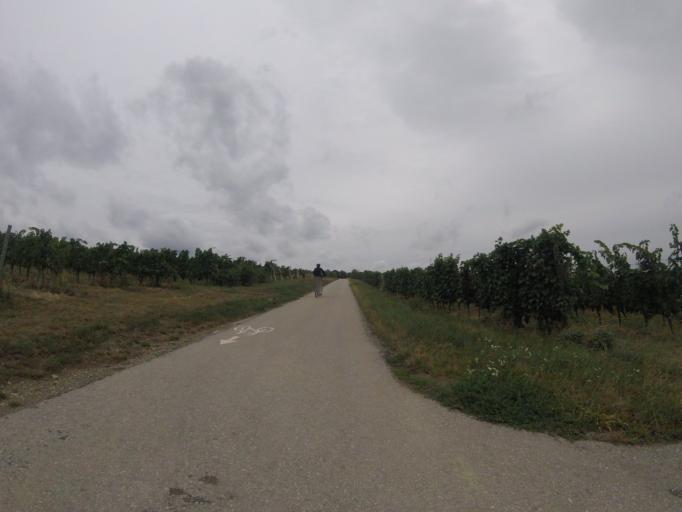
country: AT
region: Burgenland
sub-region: Eisenstadt-Umgebung
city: Breitenbrunn
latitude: 47.9354
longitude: 16.7069
